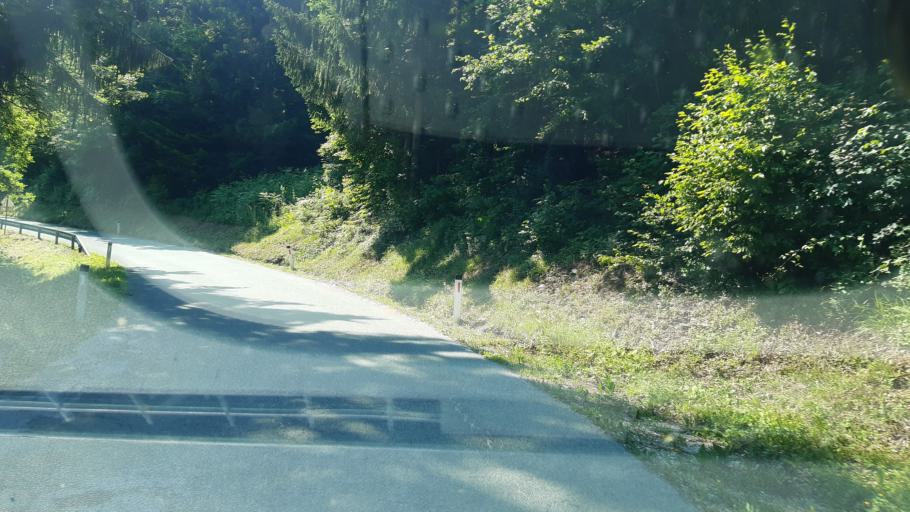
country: SI
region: Trzic
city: Bistrica pri Trzicu
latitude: 46.3598
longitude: 14.2485
